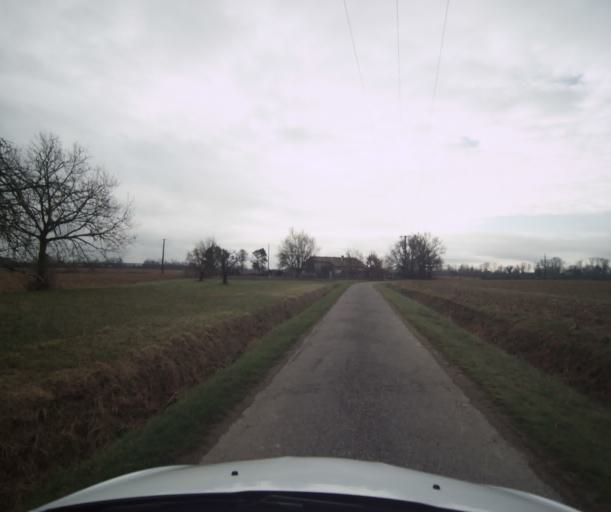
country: FR
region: Midi-Pyrenees
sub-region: Departement du Tarn-et-Garonne
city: Saint-Porquier
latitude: 44.0280
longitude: 1.1626
